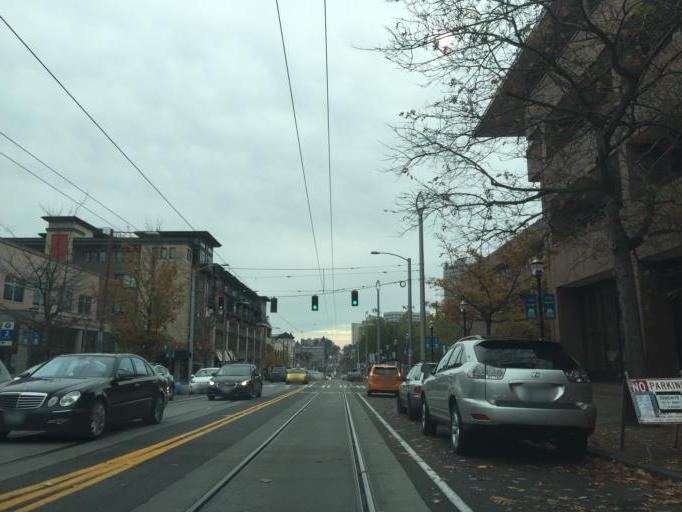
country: US
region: Washington
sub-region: King County
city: Seattle
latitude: 47.6169
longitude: -122.3209
